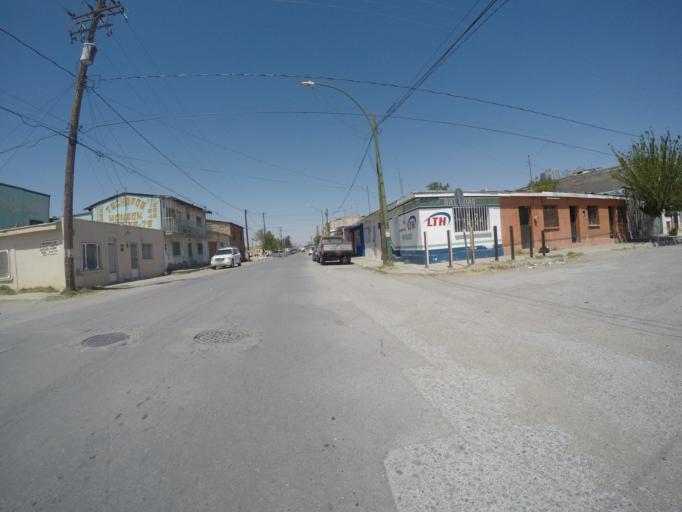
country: MX
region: Chihuahua
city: Ciudad Juarez
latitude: 31.7296
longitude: -106.4812
